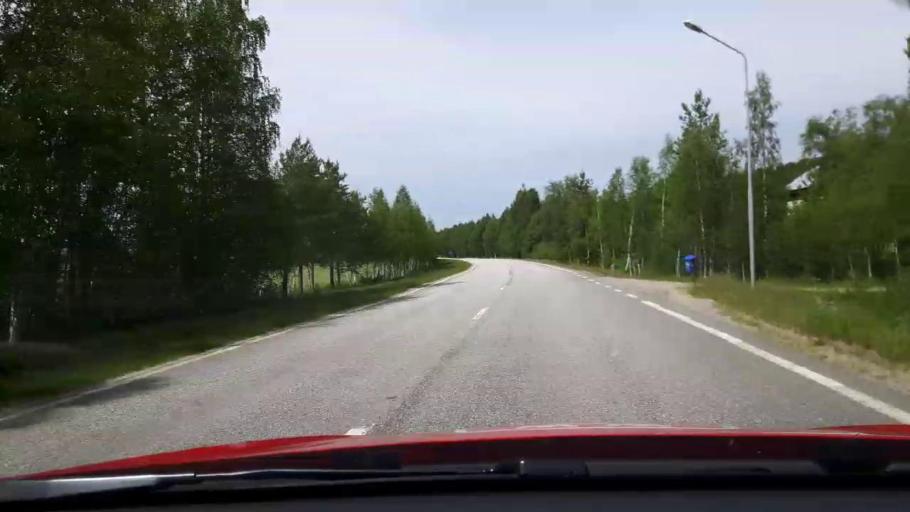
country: SE
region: Jaemtland
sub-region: Harjedalens Kommun
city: Sveg
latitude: 62.1277
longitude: 14.0664
